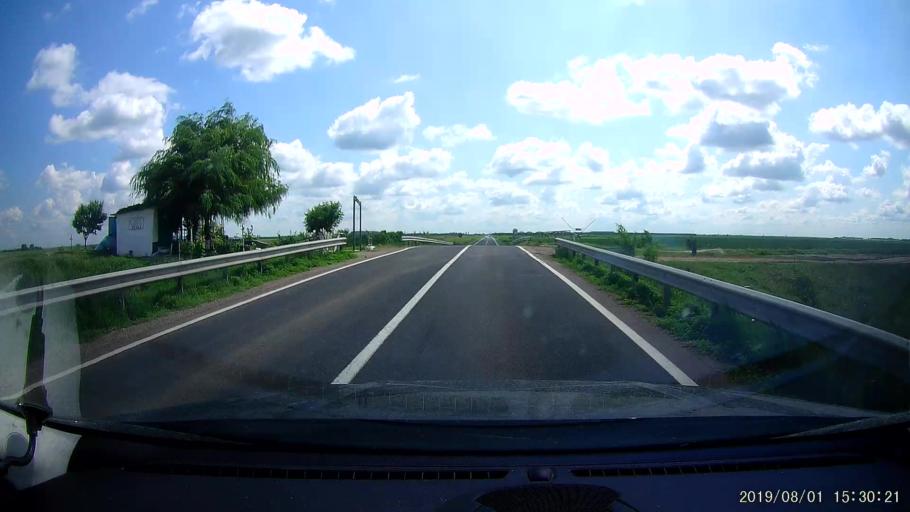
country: RO
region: Braila
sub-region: Comuna Viziru
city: Viziru
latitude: 44.9651
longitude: 27.6792
